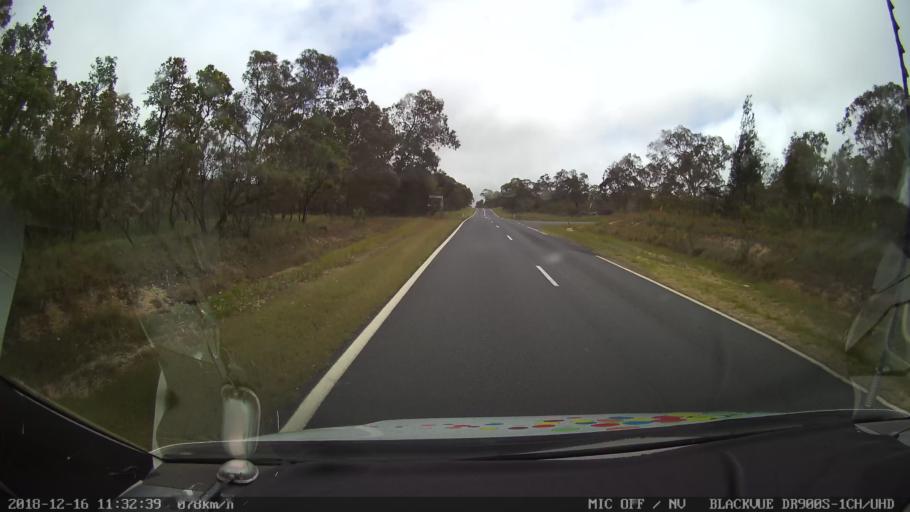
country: AU
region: New South Wales
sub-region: Tenterfield Municipality
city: Carrolls Creek
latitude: -29.0131
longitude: 152.1374
